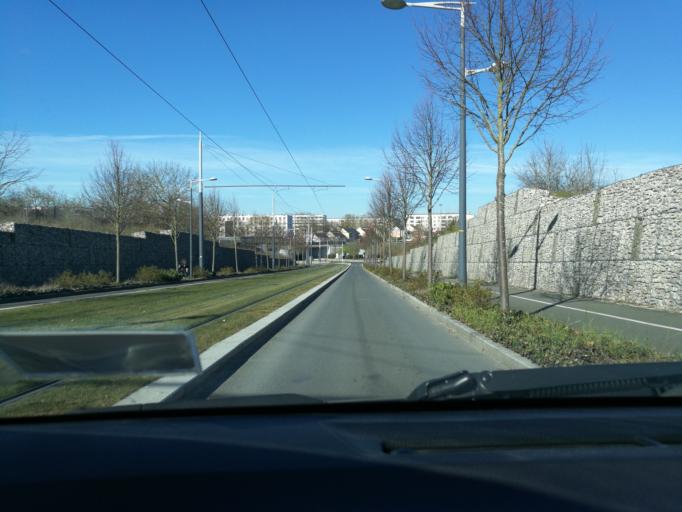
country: FR
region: Centre
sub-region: Departement du Loiret
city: Saint-Jean-de-la-Ruelle
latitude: 47.9017
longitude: 1.8741
